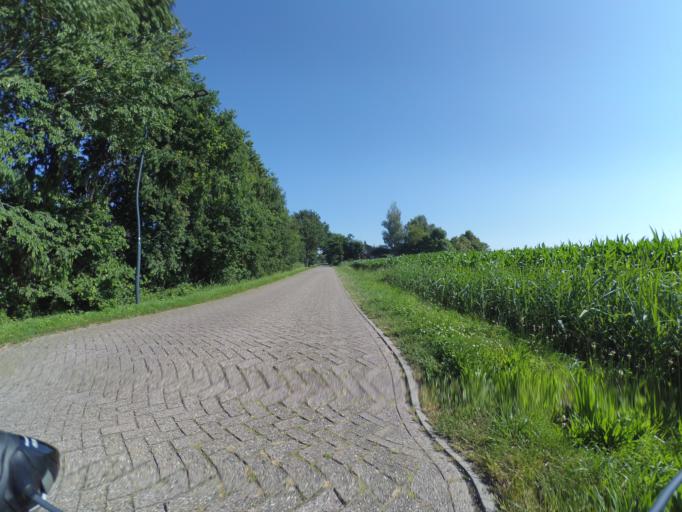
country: NL
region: North Brabant
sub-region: Gemeente Made en Drimmelen
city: Made
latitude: 51.6588
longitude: 4.7907
